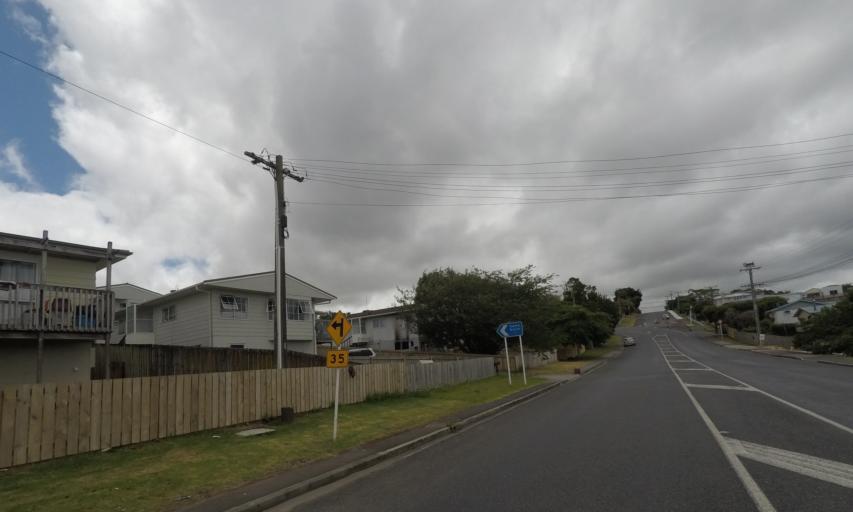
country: NZ
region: Northland
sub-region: Whangarei
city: Whangarei
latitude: -35.6778
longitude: 174.3134
